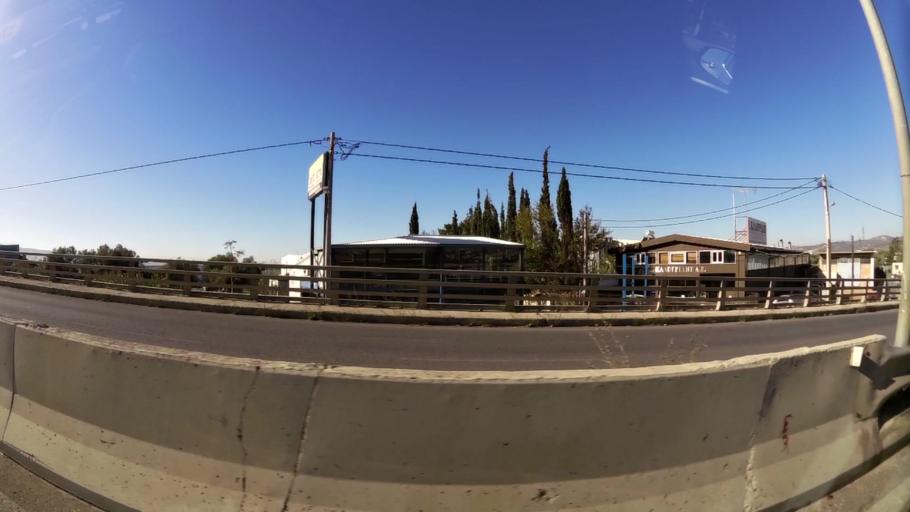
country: GR
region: Attica
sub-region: Nomarchia Athinas
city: Metamorfosi
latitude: 38.0888
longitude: 23.7599
